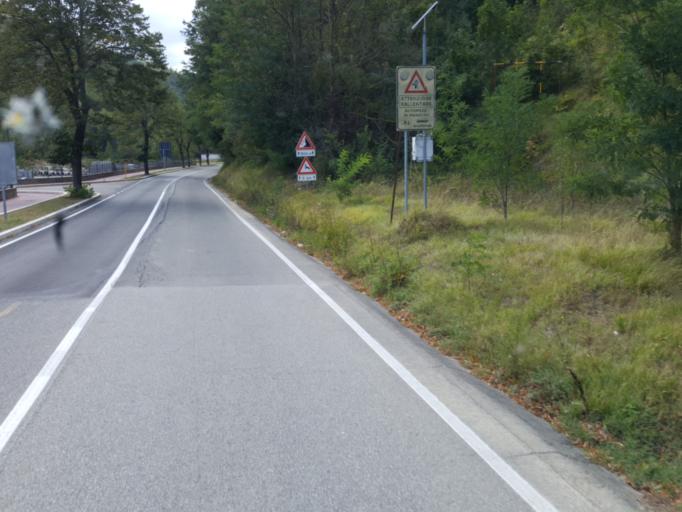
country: IT
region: Emilia-Romagna
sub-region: Forli-Cesena
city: San Piero in Bagno
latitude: 43.8453
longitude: 11.9697
